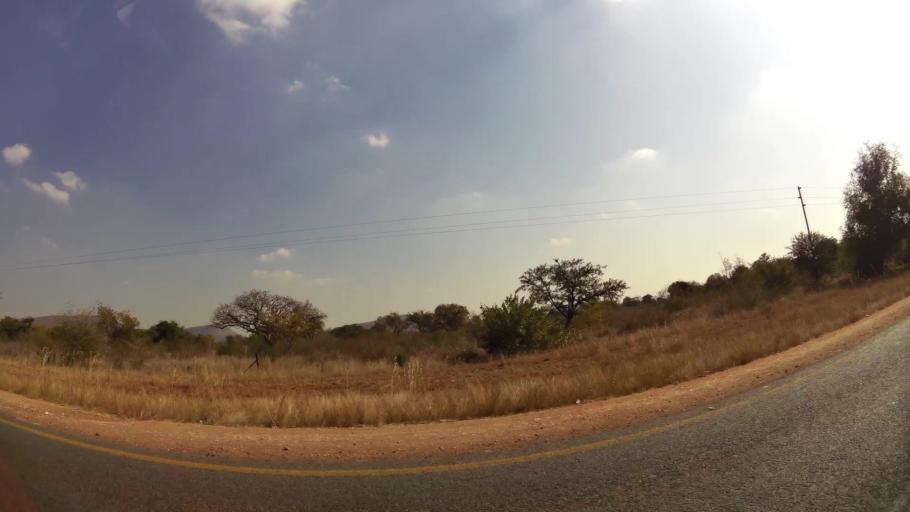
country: ZA
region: North-West
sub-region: Bojanala Platinum District Municipality
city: Mogwase
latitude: -25.4653
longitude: 27.0873
